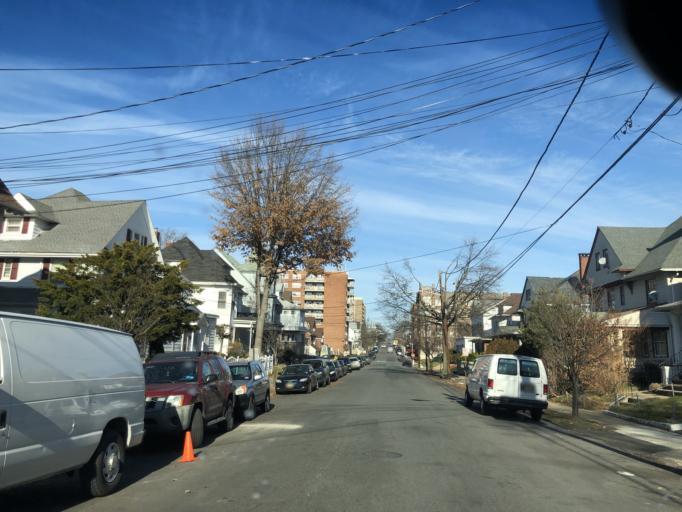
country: US
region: New Jersey
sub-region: Passaic County
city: Paterson
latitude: 40.9170
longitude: -74.1478
